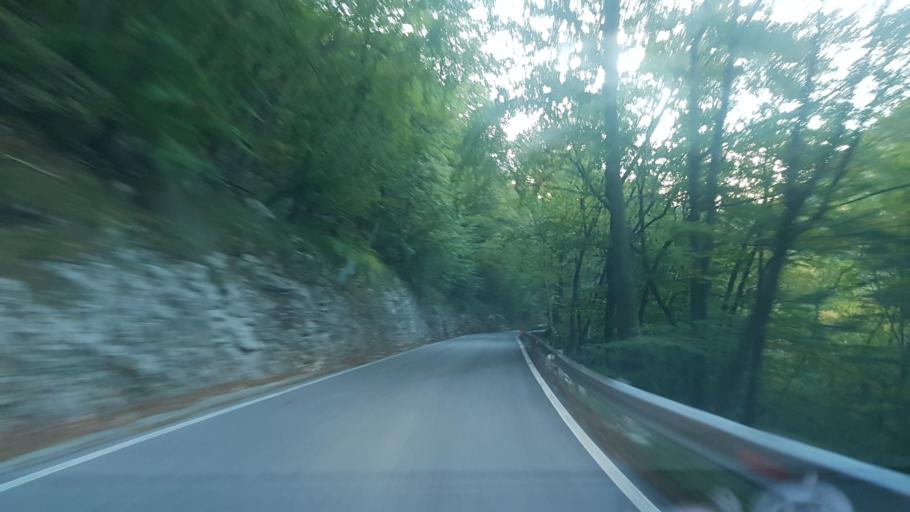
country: IT
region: Friuli Venezia Giulia
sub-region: Provincia di Udine
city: Villa Santina
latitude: 46.3506
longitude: 12.9147
